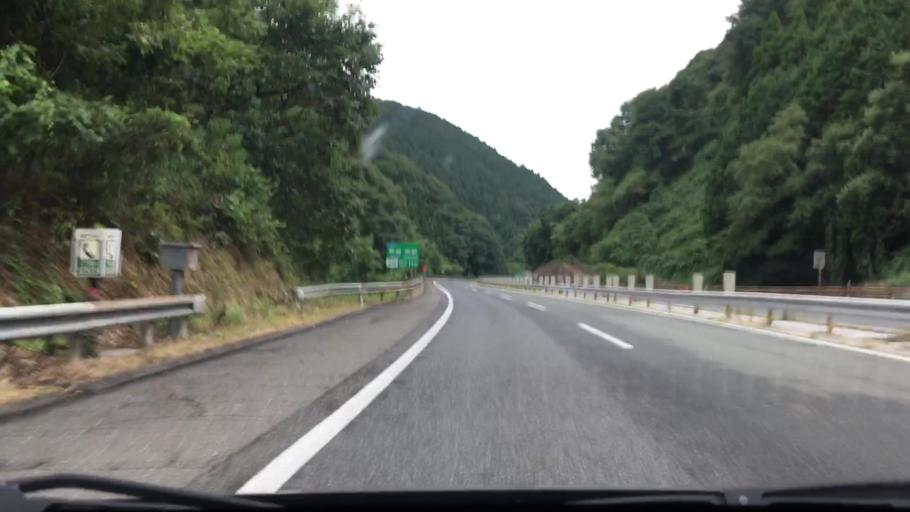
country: JP
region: Okayama
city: Niimi
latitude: 34.8955
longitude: 133.2890
